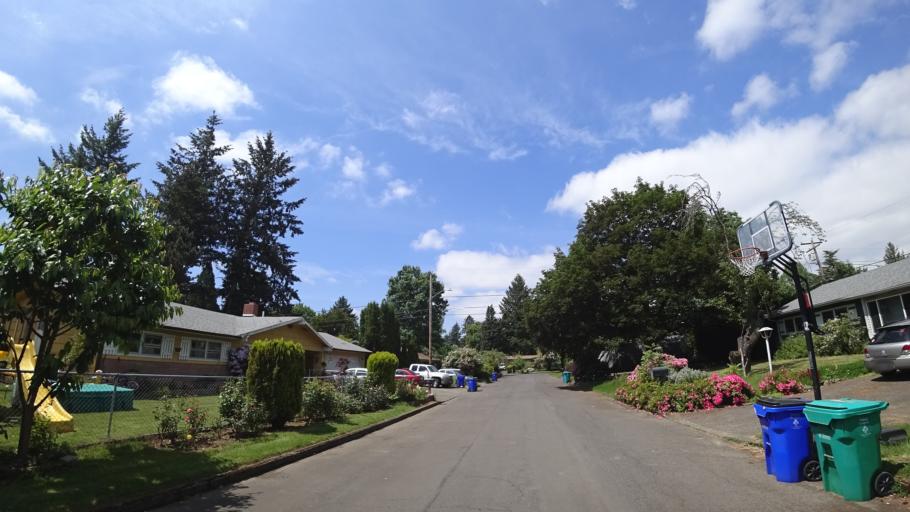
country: US
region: Oregon
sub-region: Multnomah County
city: Gresham
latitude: 45.4992
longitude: -122.4918
